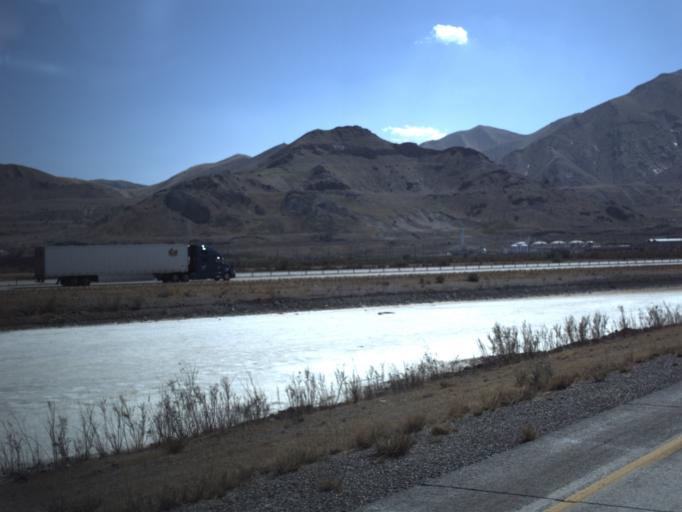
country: US
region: Utah
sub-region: Salt Lake County
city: Magna
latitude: 40.7446
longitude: -112.1856
